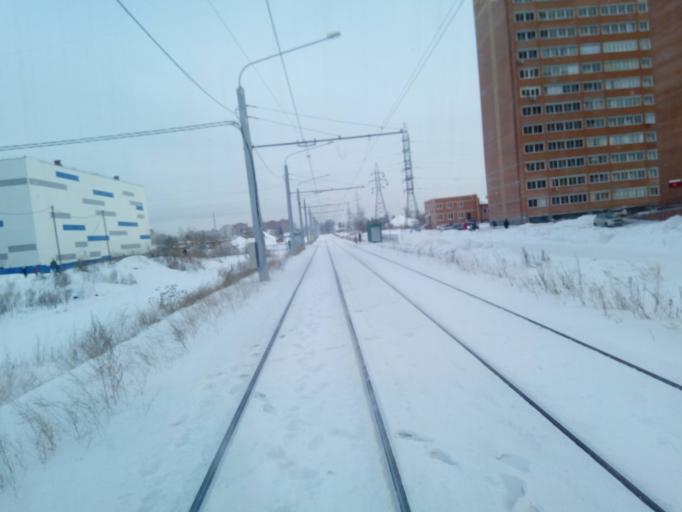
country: RU
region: Novosibirsk
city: Tolmachevo
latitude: 54.9790
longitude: 82.8103
